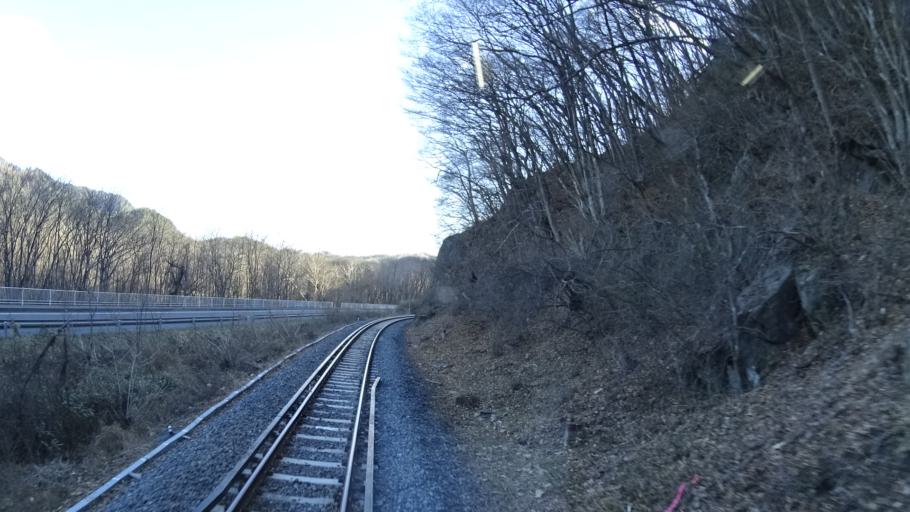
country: JP
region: Iwate
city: Yamada
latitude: 39.5528
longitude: 141.9398
